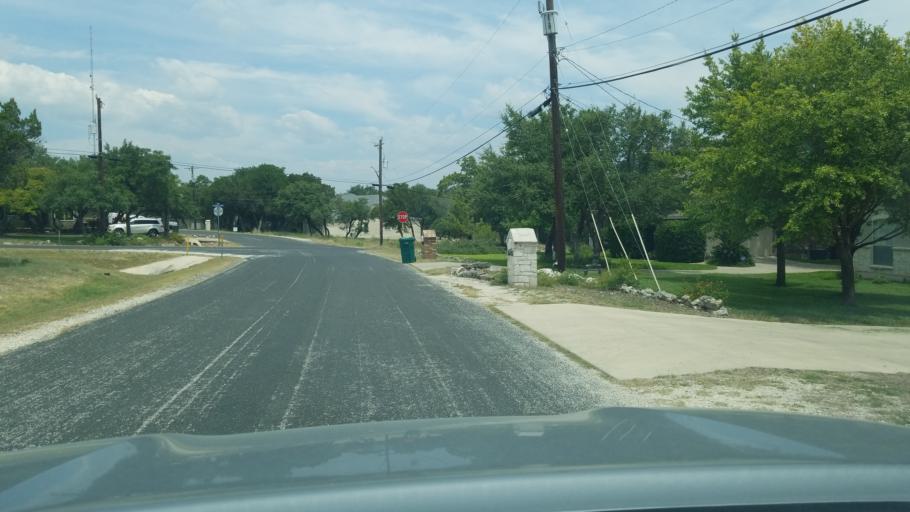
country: US
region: Texas
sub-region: Bexar County
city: Timberwood Park
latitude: 29.6914
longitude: -98.5078
